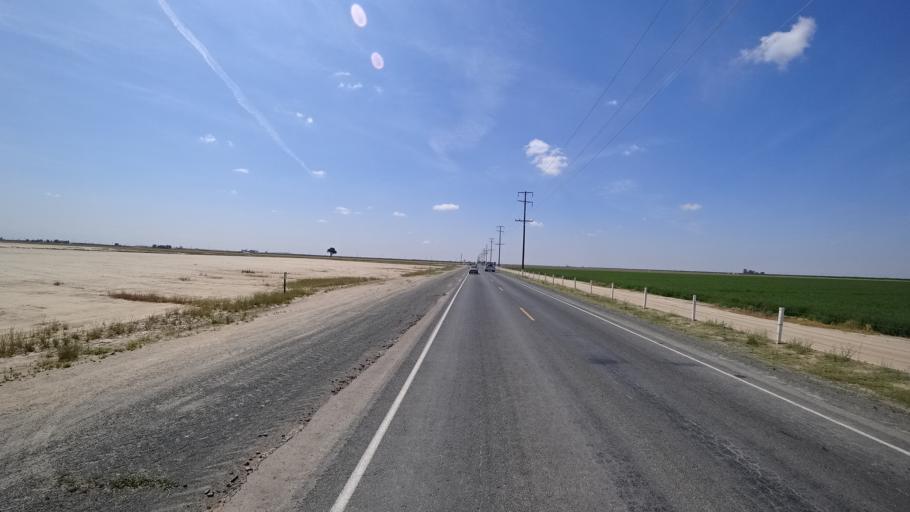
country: US
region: California
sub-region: Tulare County
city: Goshen
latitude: 36.2930
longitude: -119.4921
